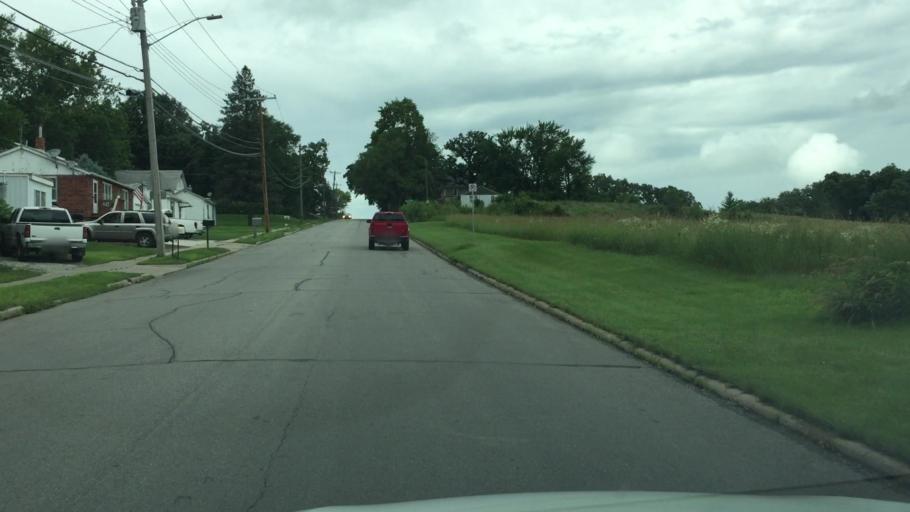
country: US
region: Iowa
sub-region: Jasper County
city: Newton
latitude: 41.7112
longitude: -93.0532
